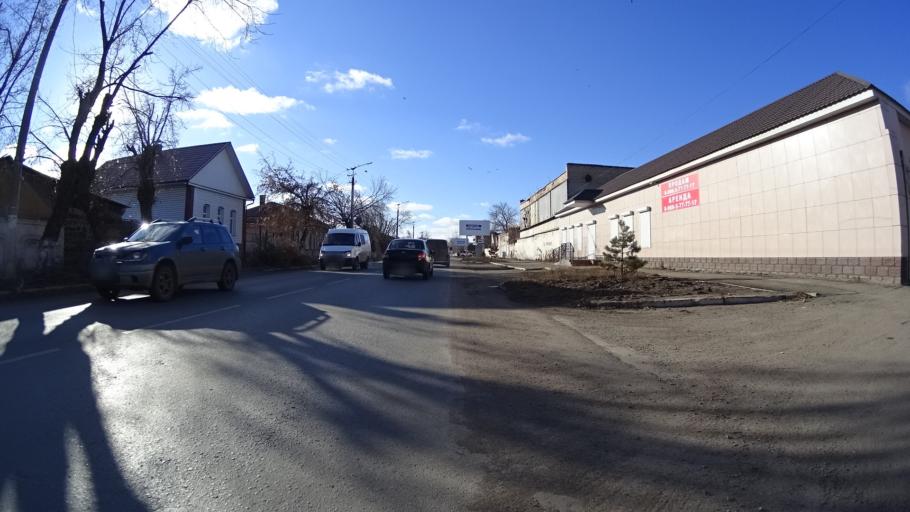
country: RU
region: Chelyabinsk
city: Troitsk
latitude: 54.0788
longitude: 61.5448
